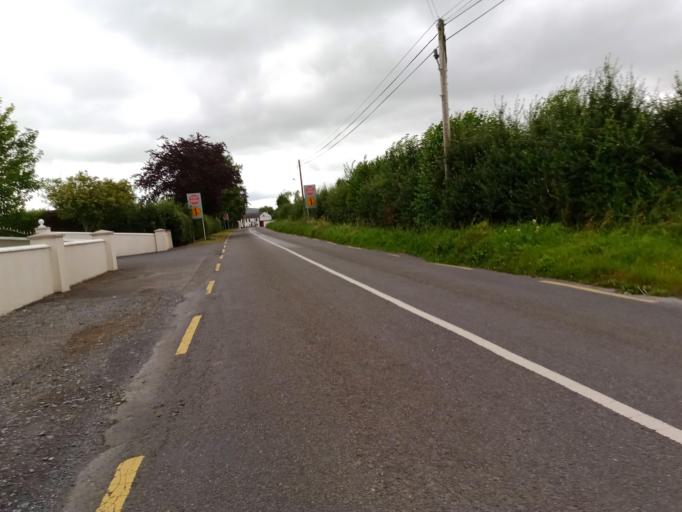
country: IE
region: Leinster
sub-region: Kilkenny
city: Callan
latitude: 52.5709
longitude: -7.4140
